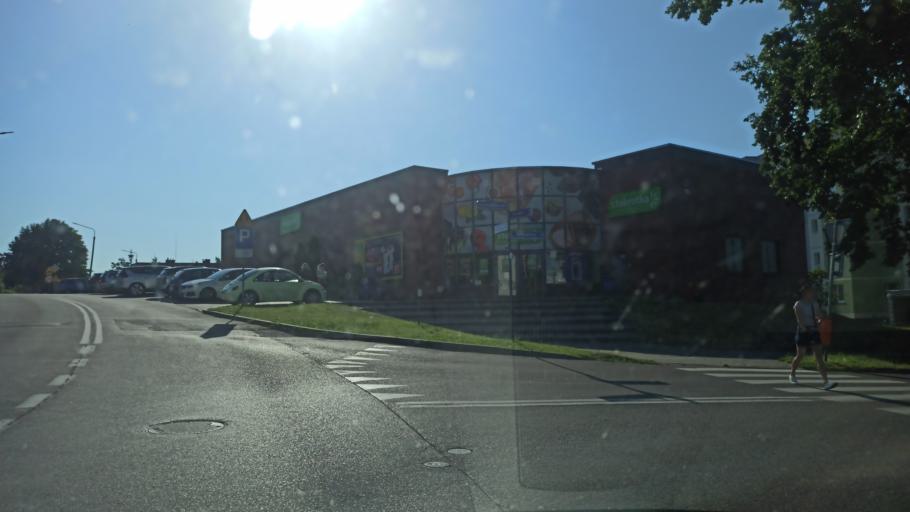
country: PL
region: Warmian-Masurian Voivodeship
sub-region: Powiat elblaski
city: Elblag
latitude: 54.1840
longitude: 19.4006
